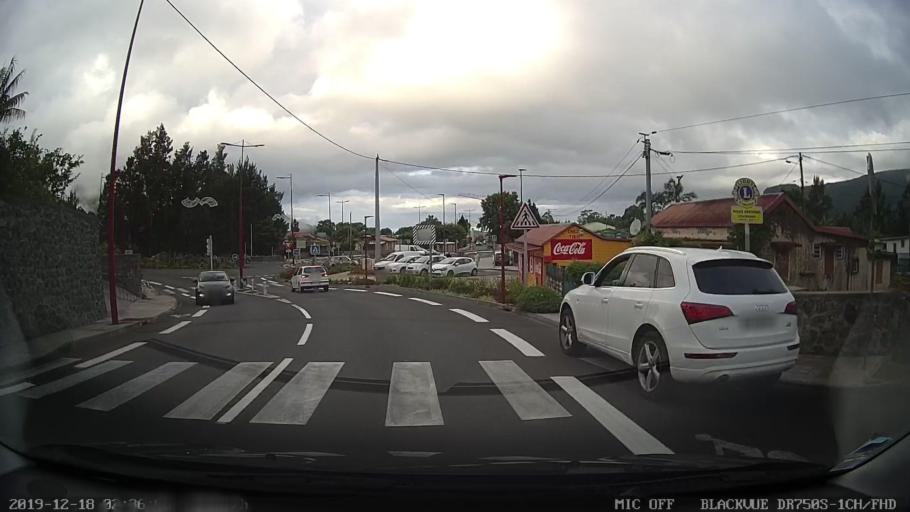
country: RE
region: Reunion
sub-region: Reunion
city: Salazie
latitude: -21.1437
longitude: 55.6202
